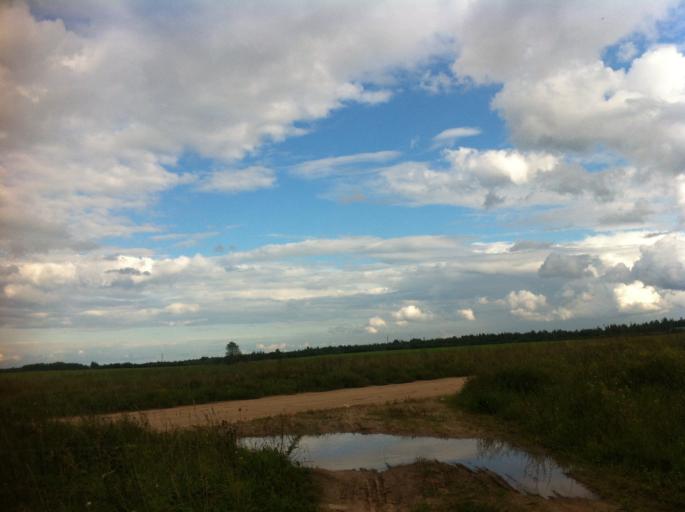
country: RU
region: Pskov
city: Izborsk
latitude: 57.8180
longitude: 27.9780
